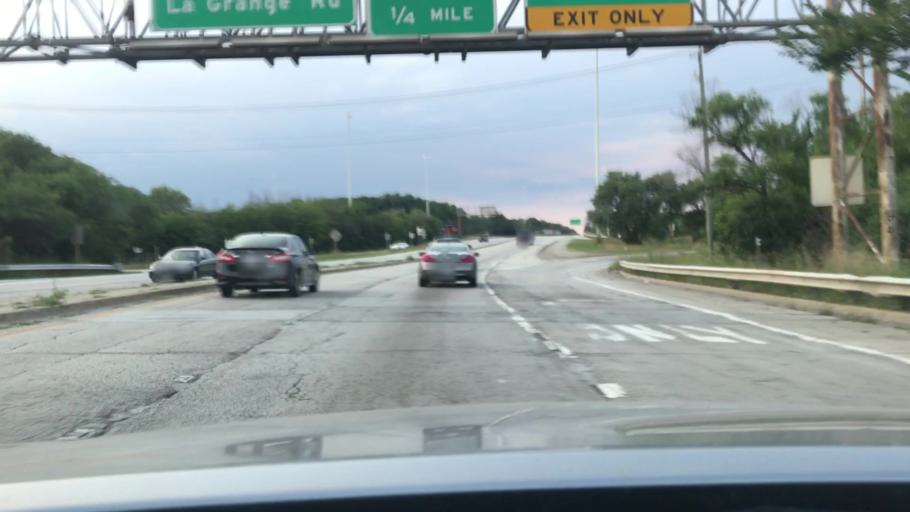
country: US
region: Illinois
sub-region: Cook County
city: Hodgkins
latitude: 41.7591
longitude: -87.8672
